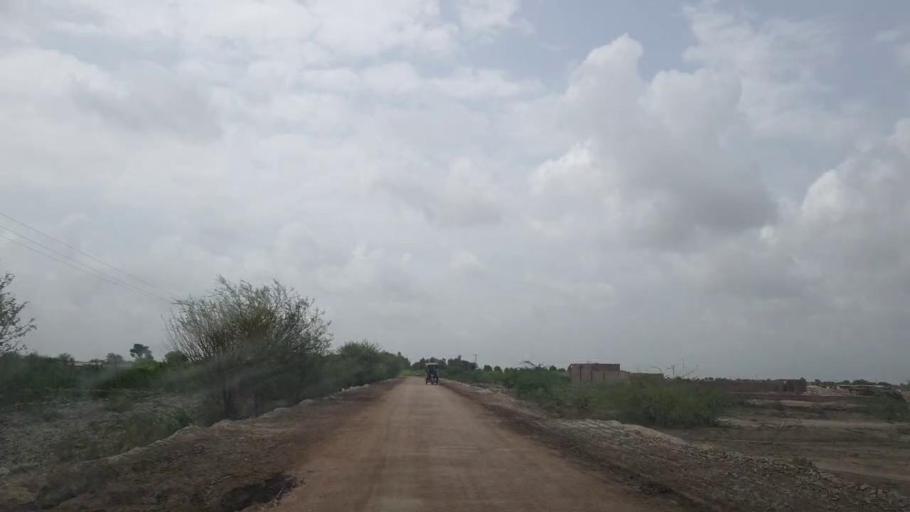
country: PK
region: Sindh
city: Naukot
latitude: 24.9445
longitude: 69.2586
